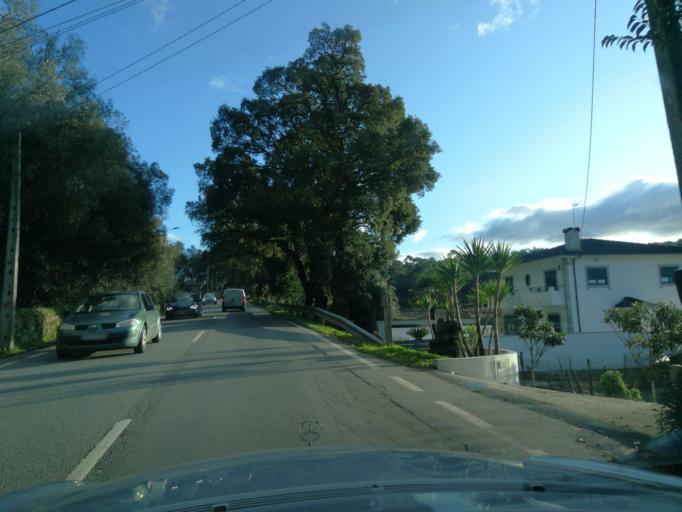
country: PT
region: Braga
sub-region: Esposende
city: Marinhas
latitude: 41.5999
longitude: -8.7398
